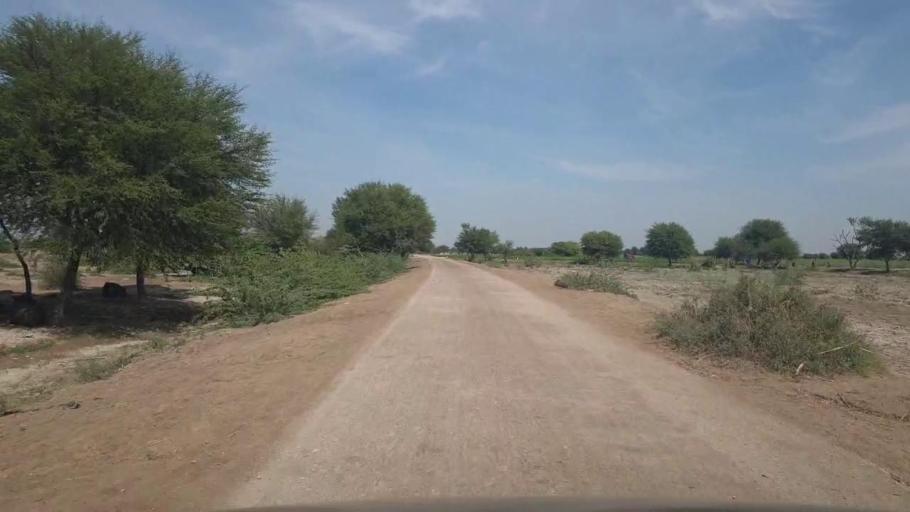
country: PK
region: Sindh
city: Kunri
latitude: 25.2132
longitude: 69.6311
